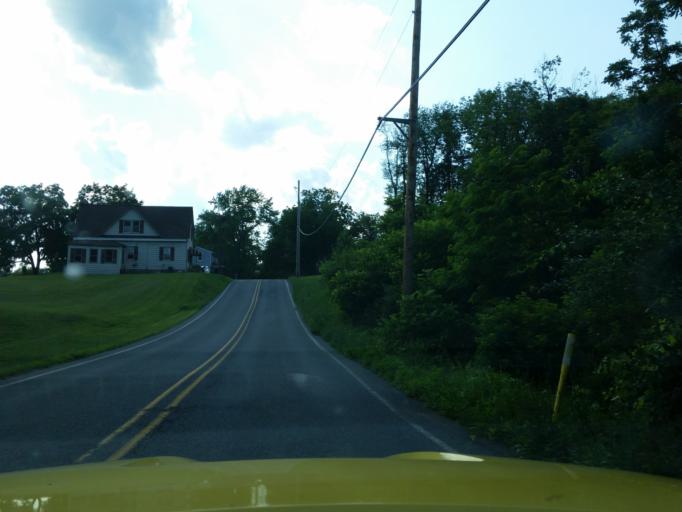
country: US
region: Pennsylvania
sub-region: Lebanon County
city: Jonestown
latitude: 40.4176
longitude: -76.5328
